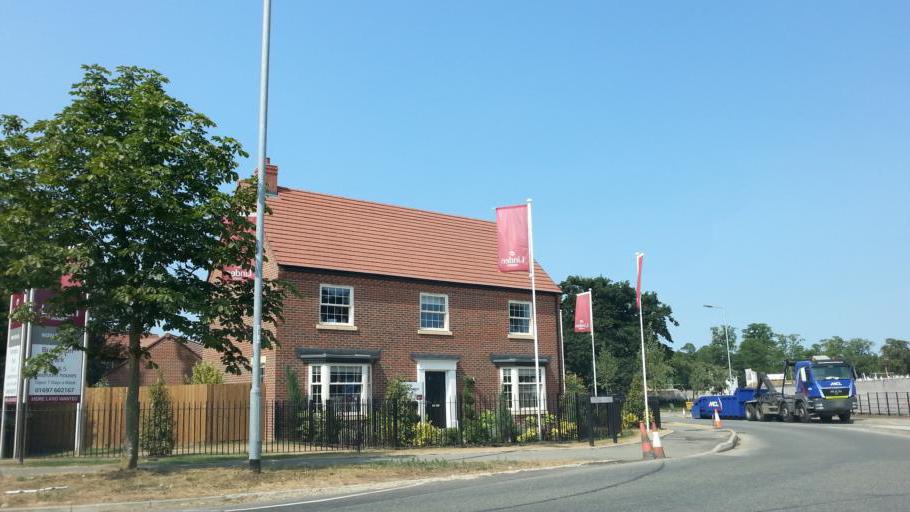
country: GB
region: England
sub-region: Cambridgeshire
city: Brampton
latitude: 52.3170
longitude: -0.2208
